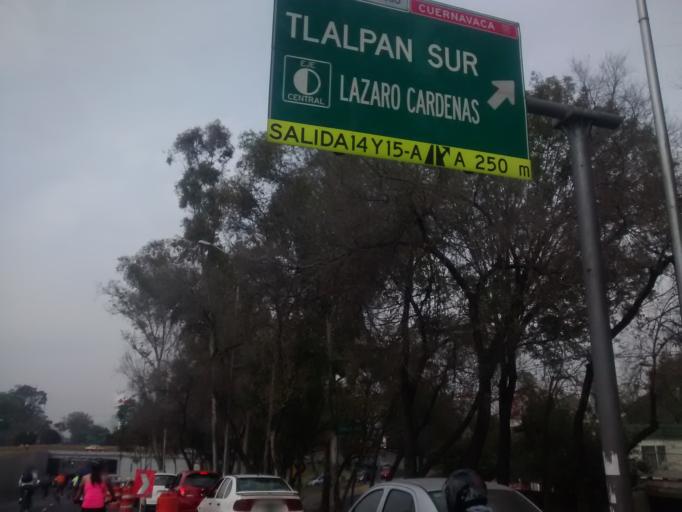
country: MX
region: Mexico City
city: Coyoacan
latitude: 19.3572
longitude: -99.1424
